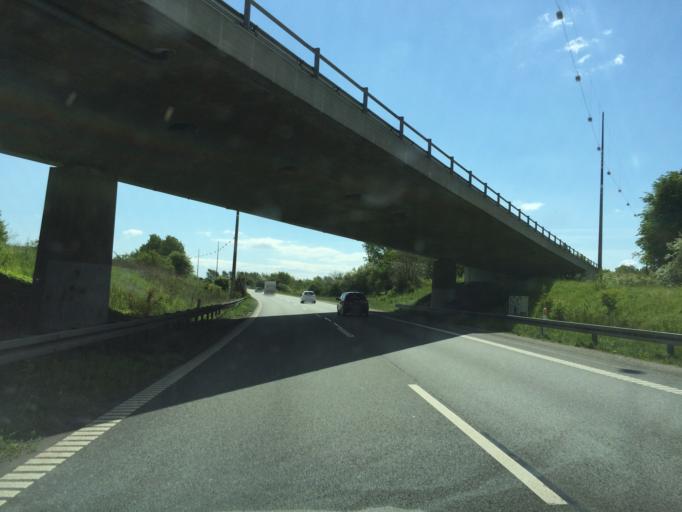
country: DK
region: Capital Region
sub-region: Albertslund Kommune
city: Albertslund
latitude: 55.6430
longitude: 12.3355
